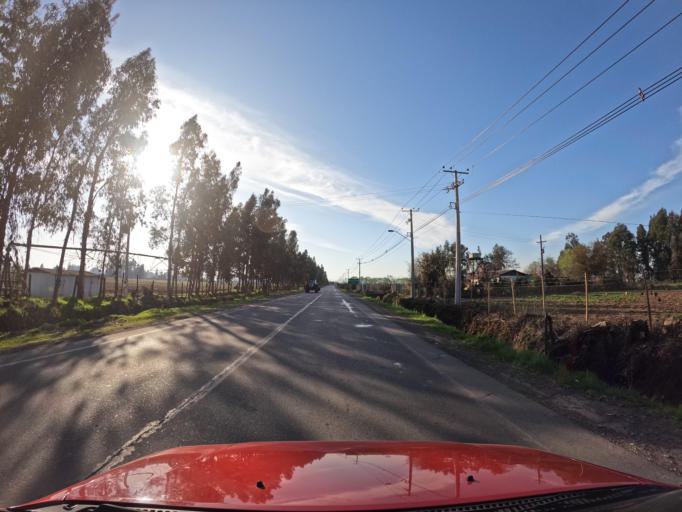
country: CL
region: Maule
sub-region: Provincia de Curico
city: Teno
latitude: -34.8765
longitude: -71.0822
